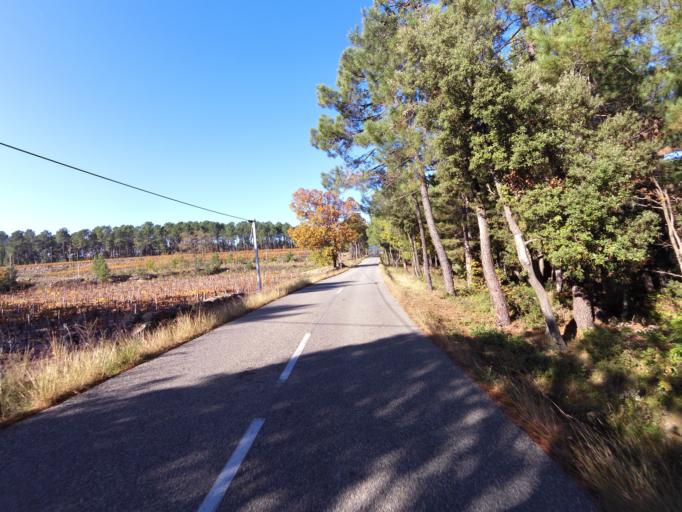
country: FR
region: Rhone-Alpes
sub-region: Departement de l'Ardeche
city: Lablachere
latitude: 44.4791
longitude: 4.1750
